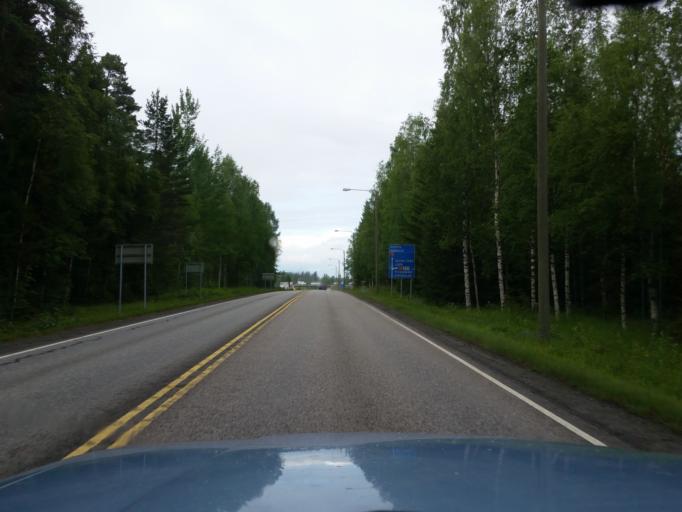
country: FI
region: Southern Savonia
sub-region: Pieksaemaeki
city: Juva
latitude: 61.8920
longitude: 27.7984
